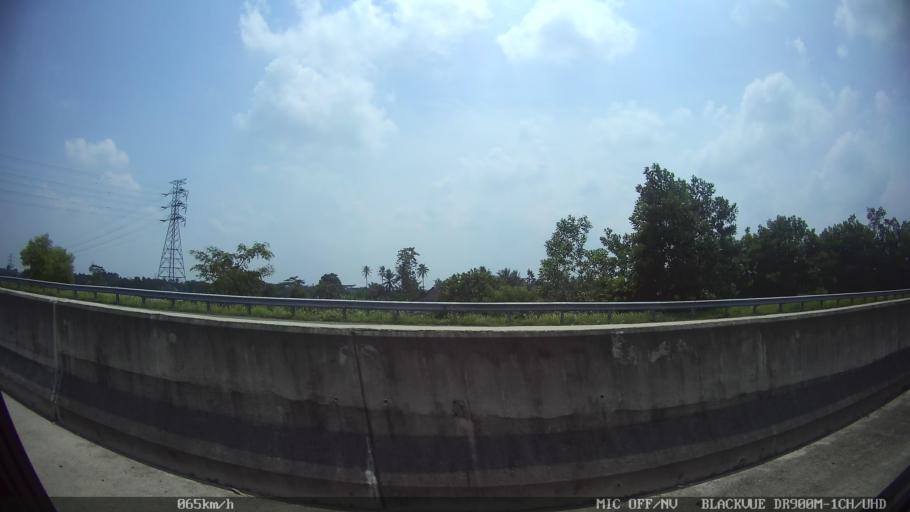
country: ID
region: Lampung
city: Kedaton
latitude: -5.3463
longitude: 105.3187
